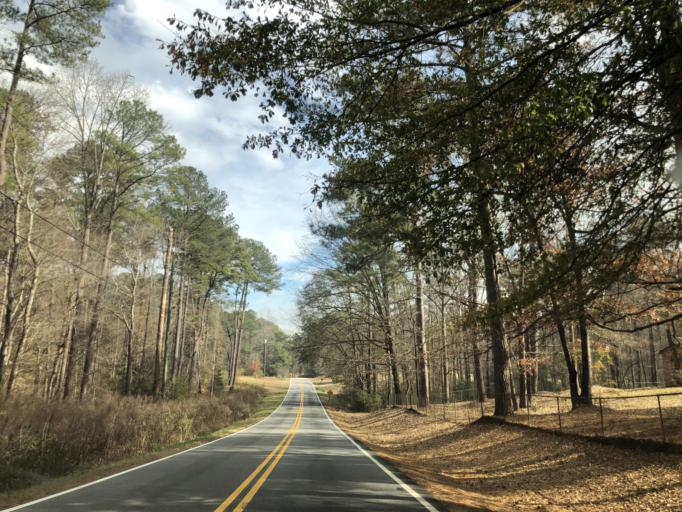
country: US
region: Georgia
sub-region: DeKalb County
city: Pine Mountain
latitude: 33.6426
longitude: -84.2009
